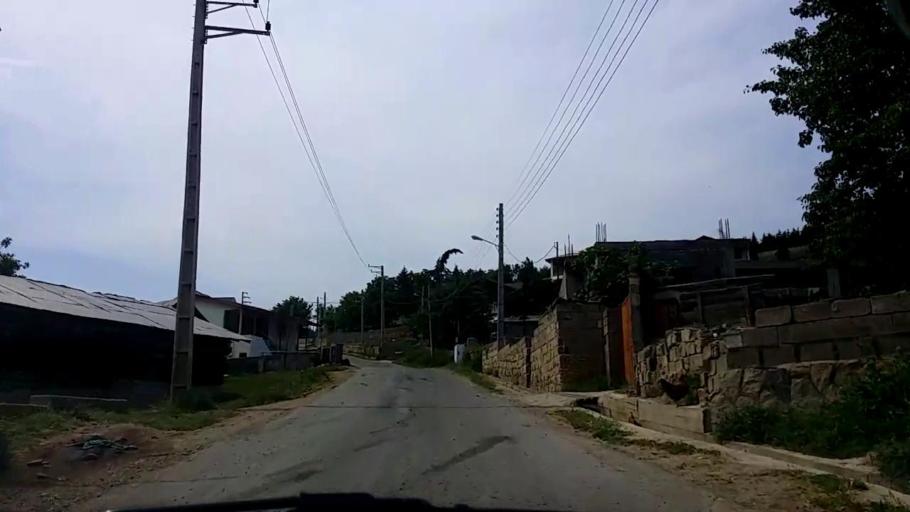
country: IR
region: Mazandaran
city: `Abbasabad
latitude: 36.5509
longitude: 51.1835
